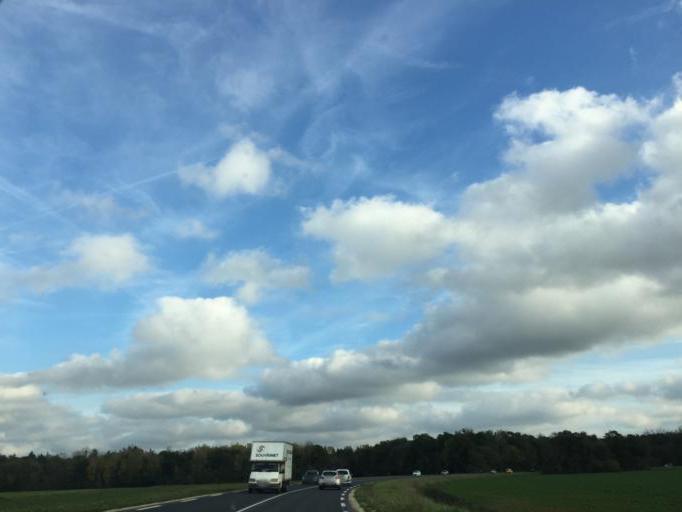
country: FR
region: Ile-de-France
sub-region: Departement de Seine-et-Marne
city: Villeneuve-le-Comte
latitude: 48.8229
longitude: 2.8388
